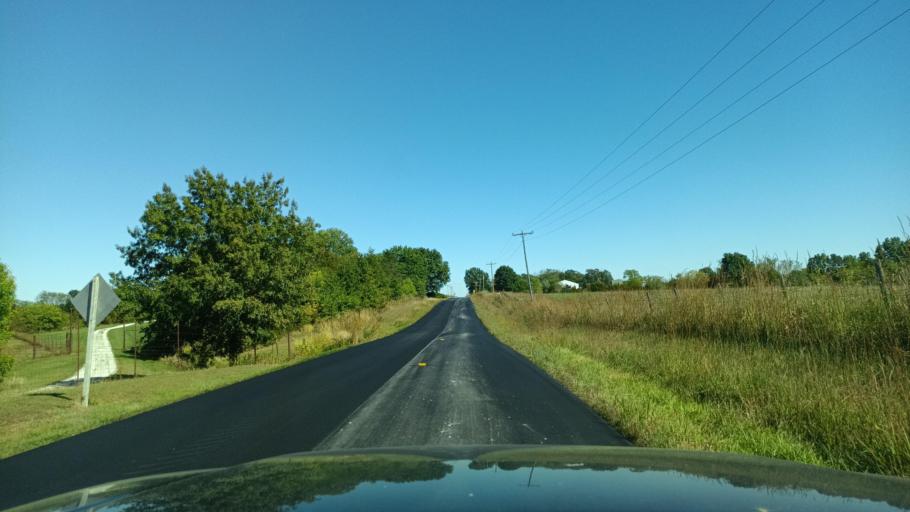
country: US
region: Missouri
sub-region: Macon County
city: La Plata
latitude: 39.9283
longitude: -92.5764
